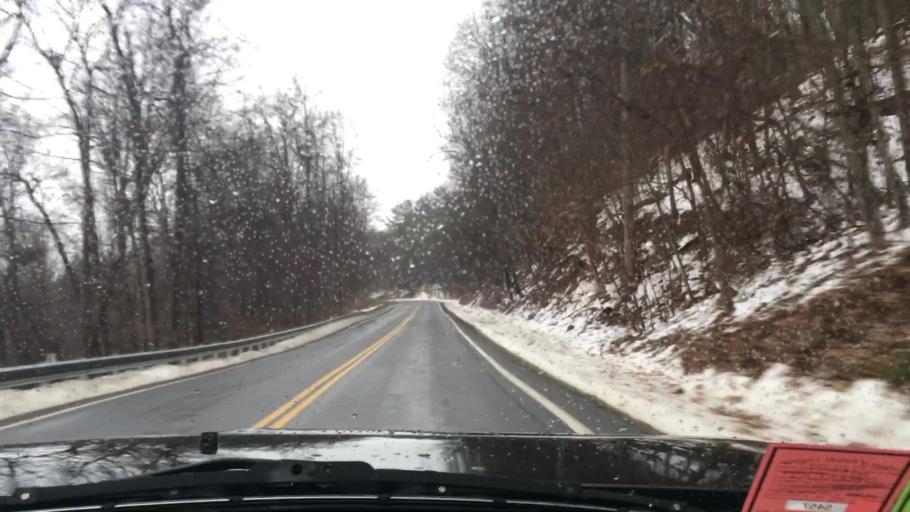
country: US
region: Virginia
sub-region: Pulaski County
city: Pulaski
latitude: 37.0135
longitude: -80.7918
